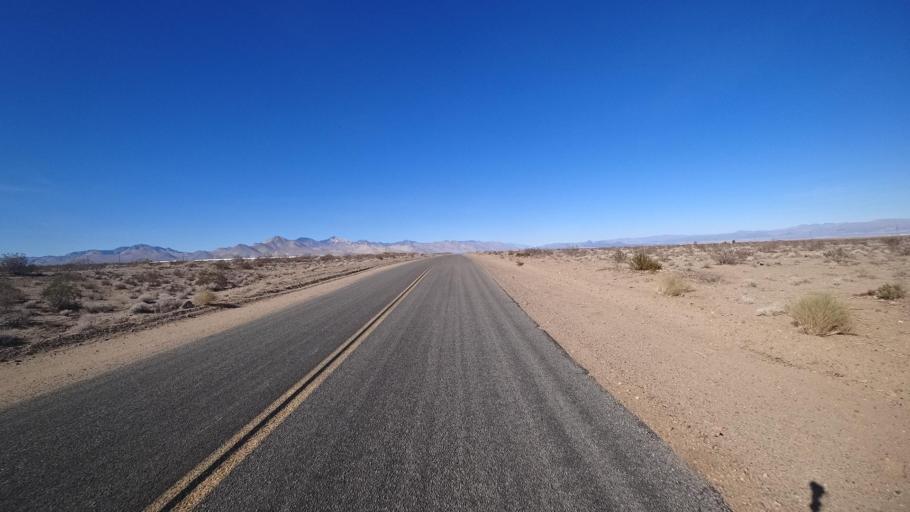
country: US
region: California
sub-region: Kern County
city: China Lake Acres
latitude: 35.5648
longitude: -117.7776
